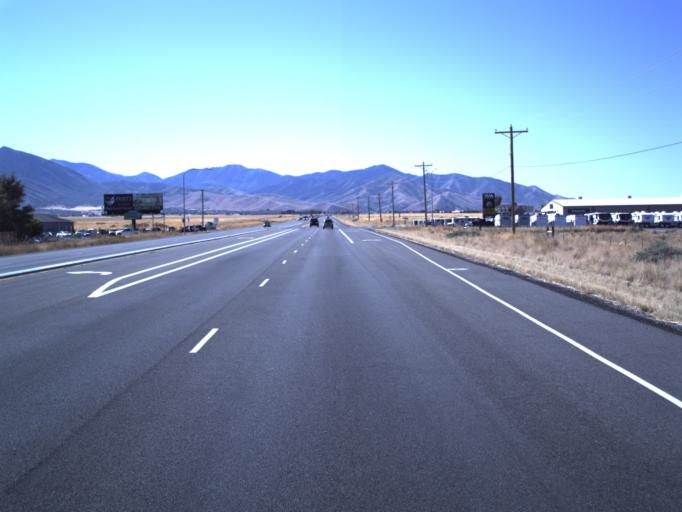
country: US
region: Utah
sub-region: Tooele County
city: Erda
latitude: 40.5954
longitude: -112.2941
